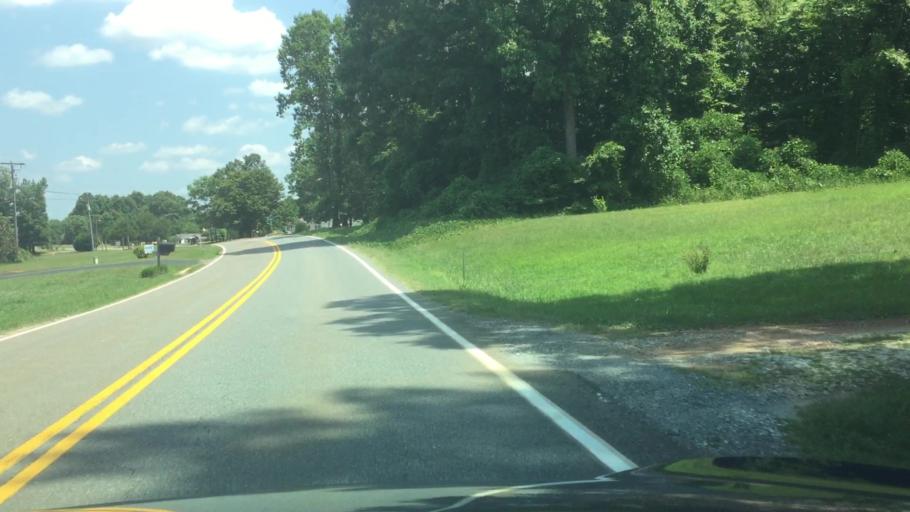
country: US
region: Virginia
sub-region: Campbell County
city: Concord
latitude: 37.3435
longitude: -78.9022
